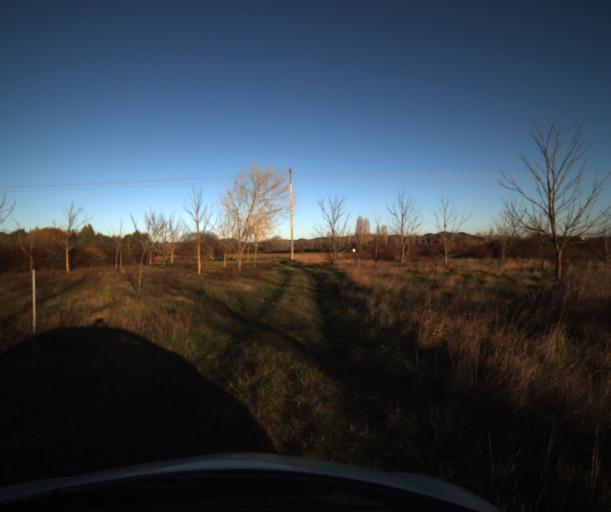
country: FR
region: Provence-Alpes-Cote d'Azur
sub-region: Departement du Vaucluse
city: Pertuis
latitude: 43.6754
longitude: 5.5146
